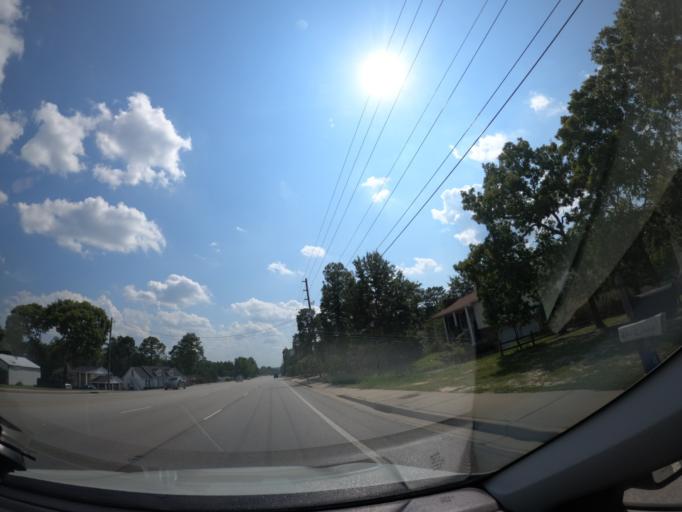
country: US
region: South Carolina
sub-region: Lexington County
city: South Congaree
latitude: 33.9336
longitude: -81.1541
